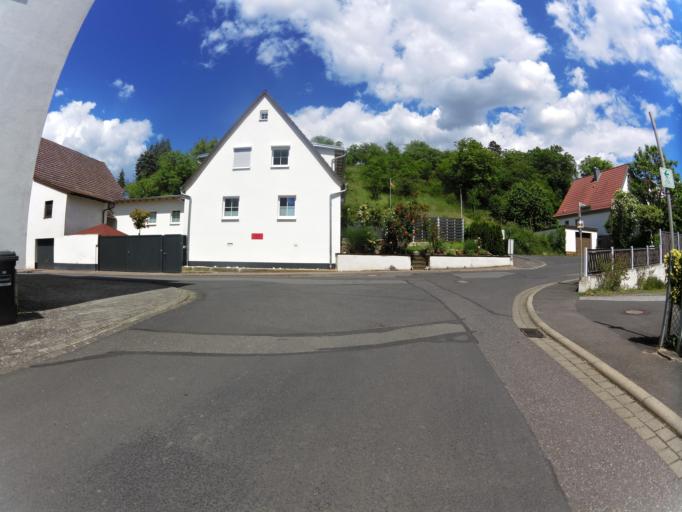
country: DE
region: Bavaria
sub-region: Regierungsbezirk Unterfranken
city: Zellingen
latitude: 49.8682
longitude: 9.8011
